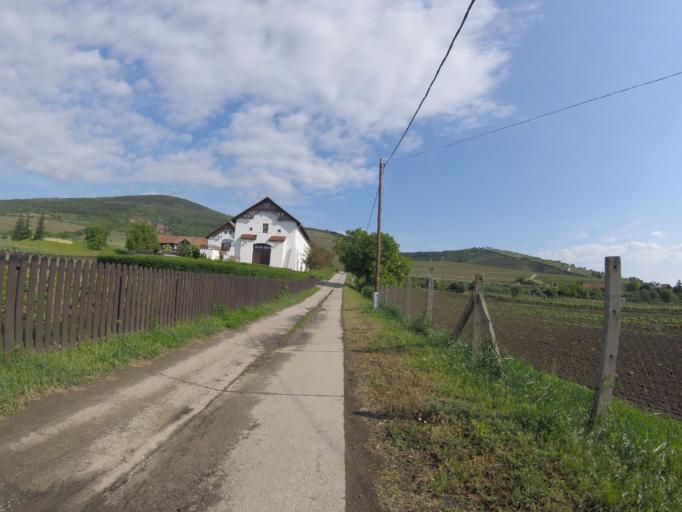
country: HU
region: Borsod-Abauj-Zemplen
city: Tokaj
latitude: 48.1086
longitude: 21.3987
